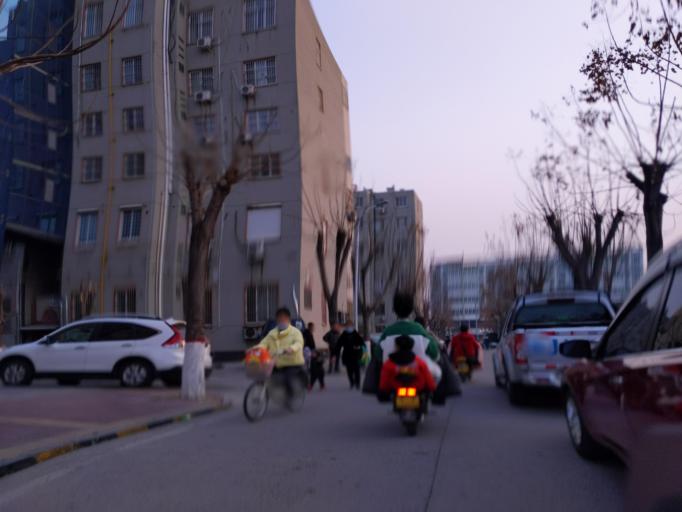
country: CN
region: Henan Sheng
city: Zhongyuanlu
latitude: 35.7717
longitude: 115.0886
